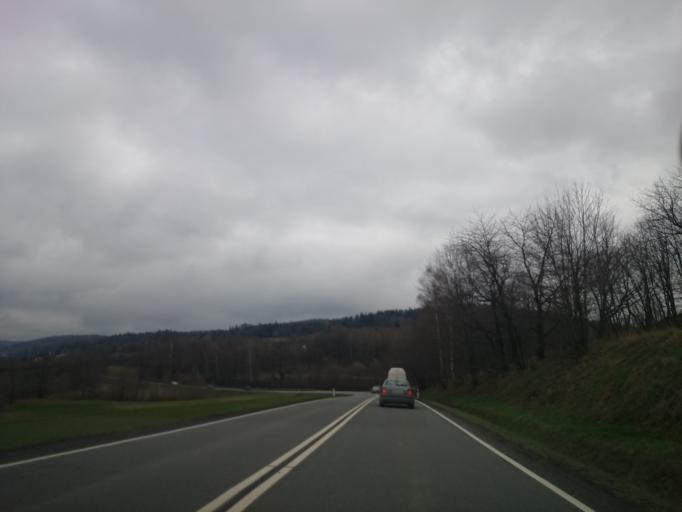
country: PL
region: Lower Silesian Voivodeship
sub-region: Powiat zabkowicki
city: Zloty Stok
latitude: 50.4519
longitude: 16.8534
